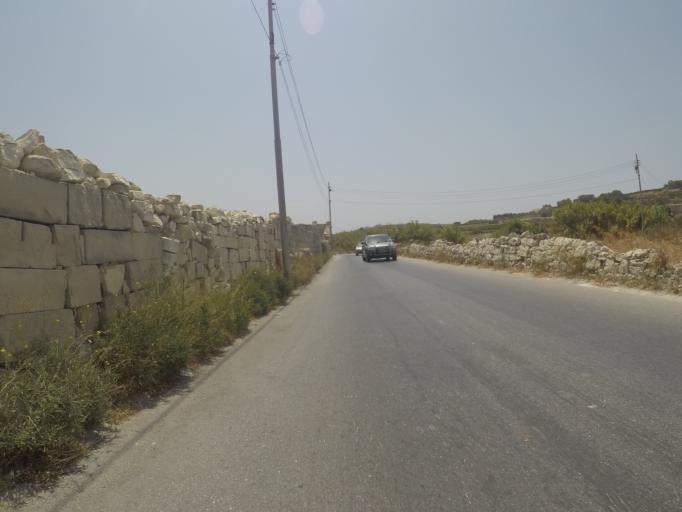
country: MT
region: Ir-Rabat
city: Rabat
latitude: 35.8703
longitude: 14.4142
